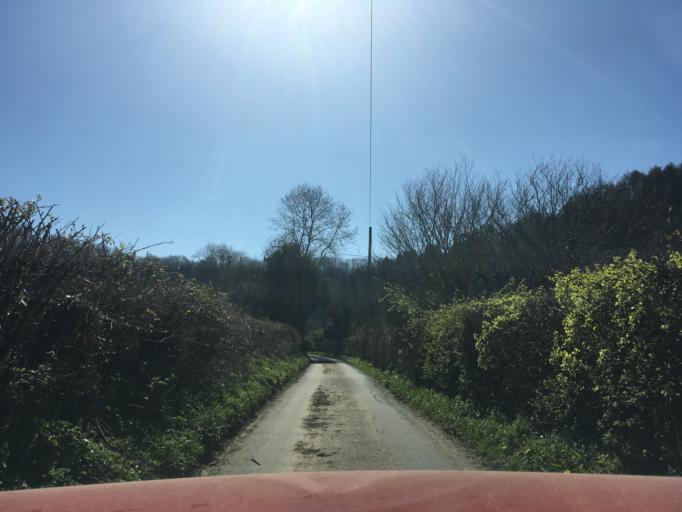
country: GB
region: England
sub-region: Gloucestershire
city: Wotton-under-Edge
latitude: 51.6537
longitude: -2.3460
